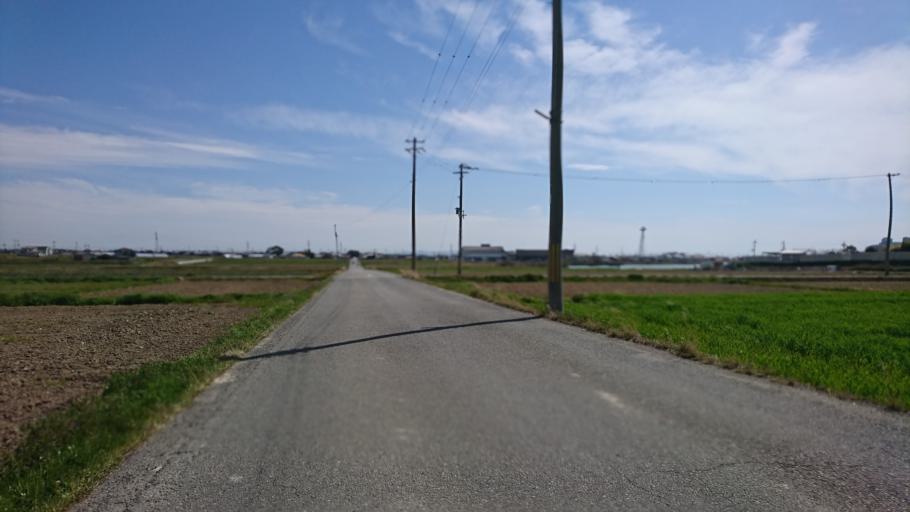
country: JP
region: Hyogo
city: Miki
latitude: 34.7604
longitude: 134.9339
